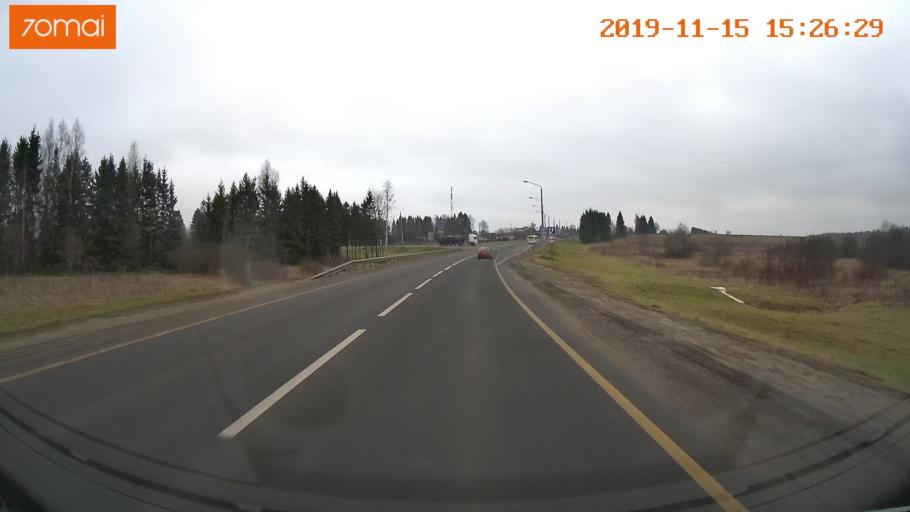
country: RU
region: Jaroslavl
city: Danilov
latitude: 58.1512
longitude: 40.1481
